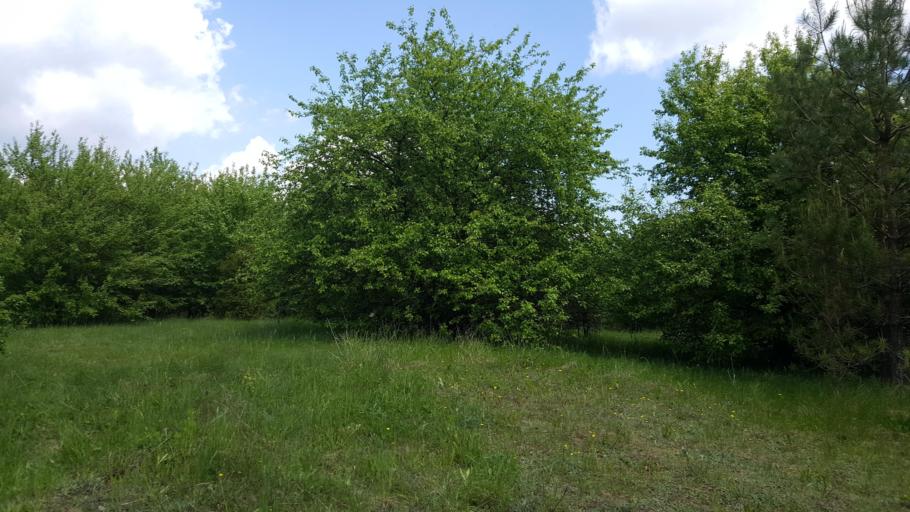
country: BY
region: Brest
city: Kamyanyets
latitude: 52.4835
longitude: 23.9642
